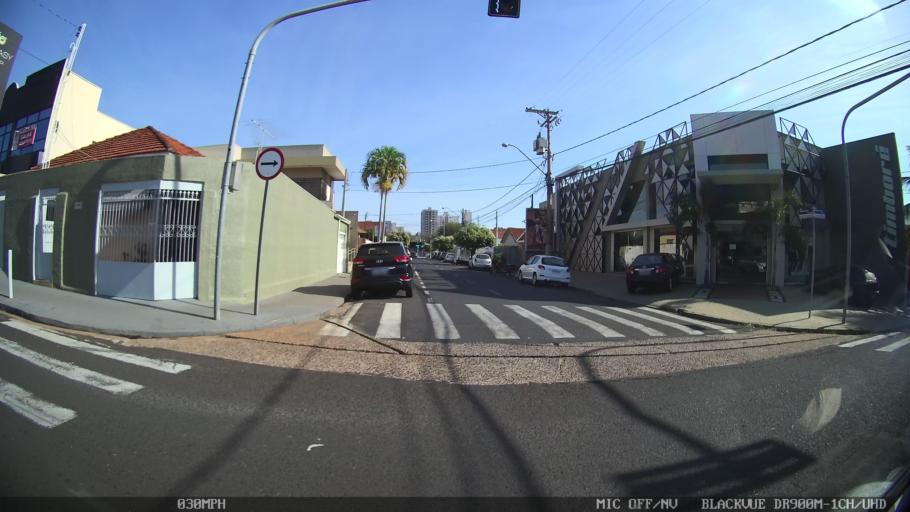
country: BR
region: Sao Paulo
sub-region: Sao Jose Do Rio Preto
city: Sao Jose do Rio Preto
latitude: -20.8210
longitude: -49.3774
